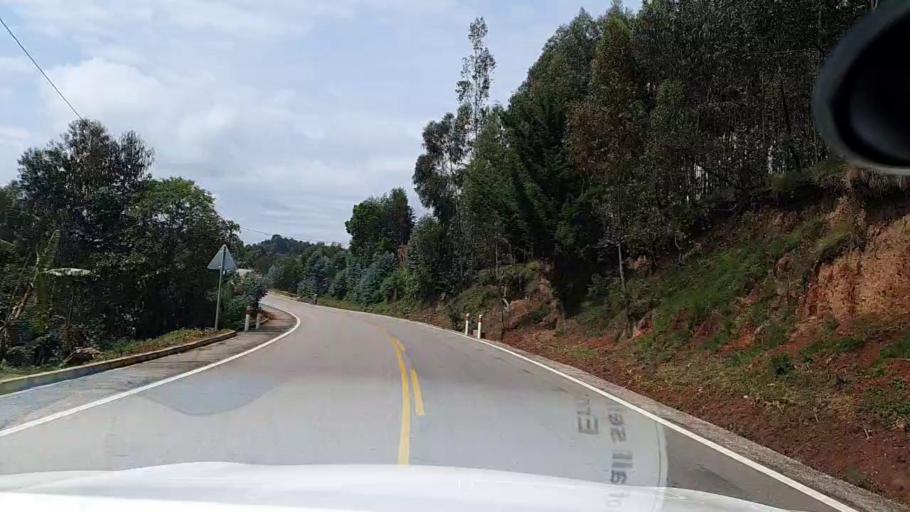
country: RW
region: Southern Province
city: Nzega
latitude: -2.4857
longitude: 29.5144
